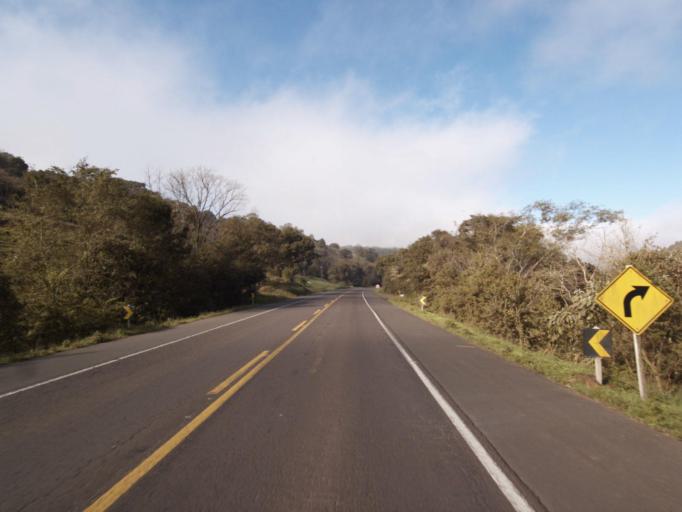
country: BR
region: Rio Grande do Sul
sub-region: Frederico Westphalen
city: Frederico Westphalen
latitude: -27.0070
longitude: -53.2248
